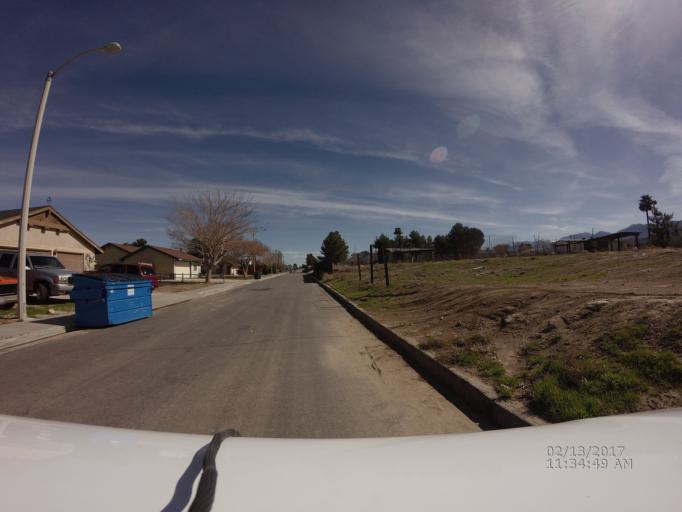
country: US
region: California
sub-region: Los Angeles County
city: Littlerock
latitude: 34.5229
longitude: -118.0002
